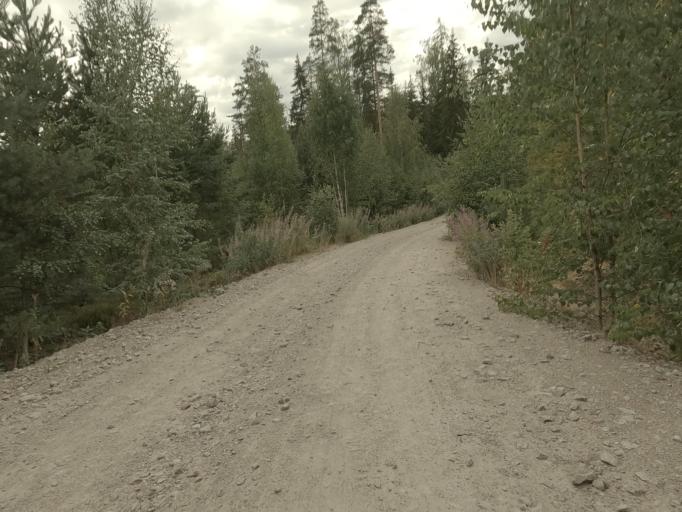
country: RU
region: Leningrad
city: Kamennogorsk
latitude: 60.9822
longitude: 29.1755
